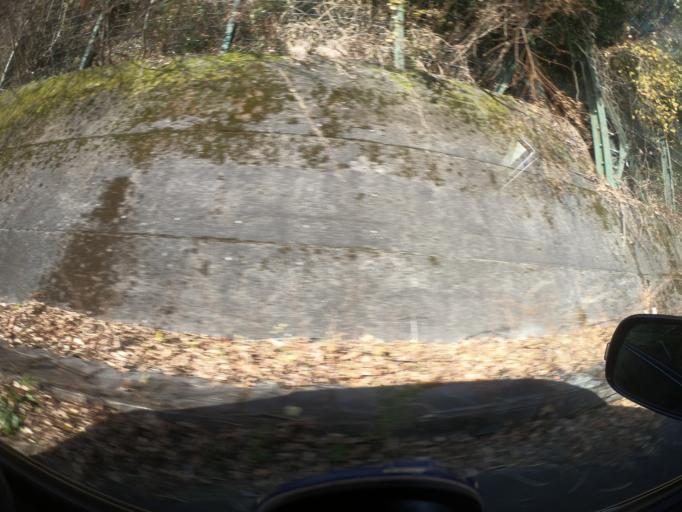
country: JP
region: Shizuoka
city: Kanaya
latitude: 35.0593
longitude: 138.0880
